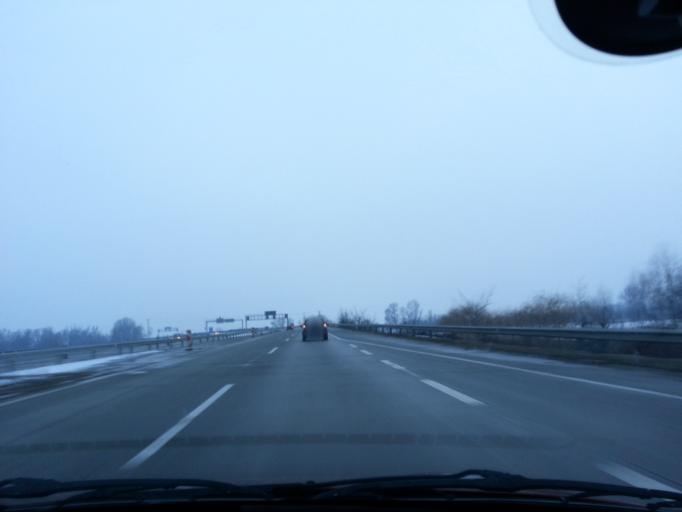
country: HU
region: Pest
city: Vecses
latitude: 47.3987
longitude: 19.3083
